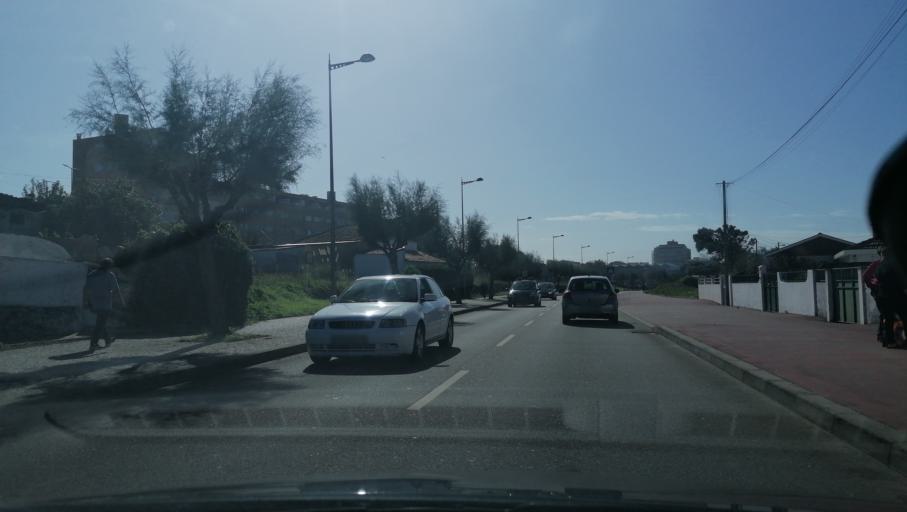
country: PT
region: Aveiro
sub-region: Espinho
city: Espinho
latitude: 41.0177
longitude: -8.6402
